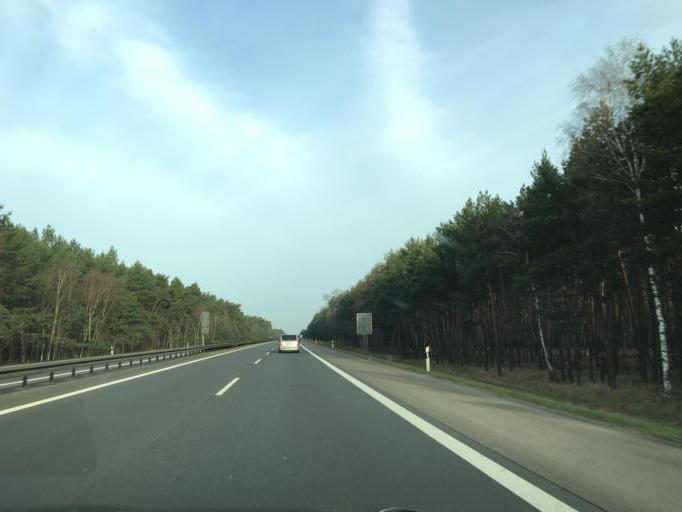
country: DE
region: Brandenburg
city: Birkenwerder
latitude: 52.6854
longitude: 13.3356
